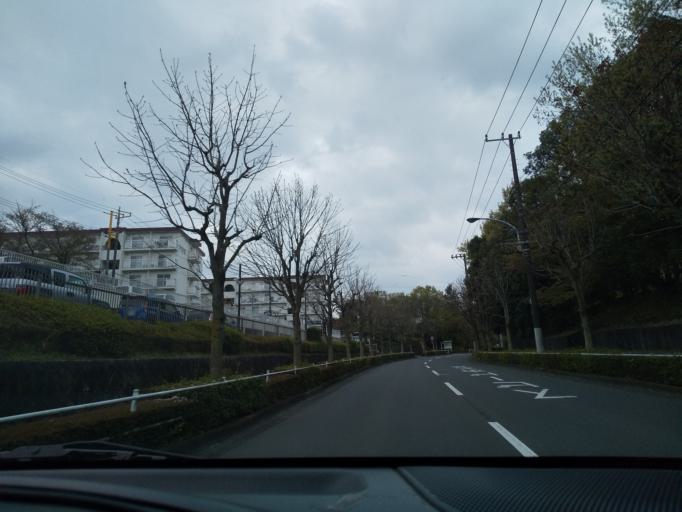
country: JP
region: Tokyo
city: Hino
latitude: 35.6071
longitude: 139.3819
